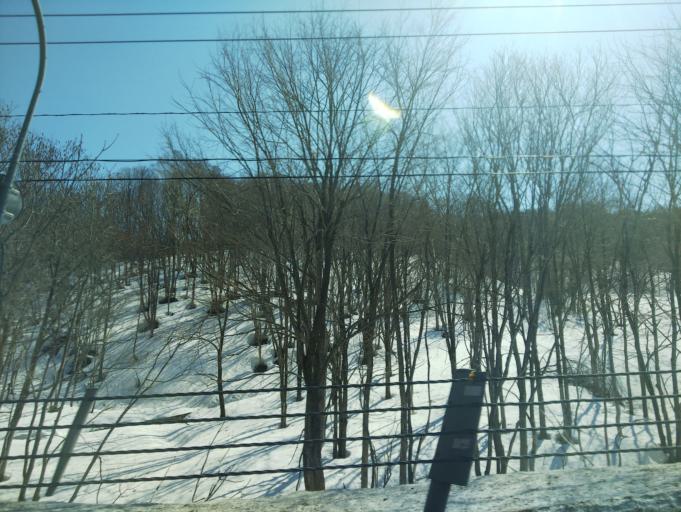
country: JP
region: Hokkaido
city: Nayoro
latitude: 44.7079
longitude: 142.2749
